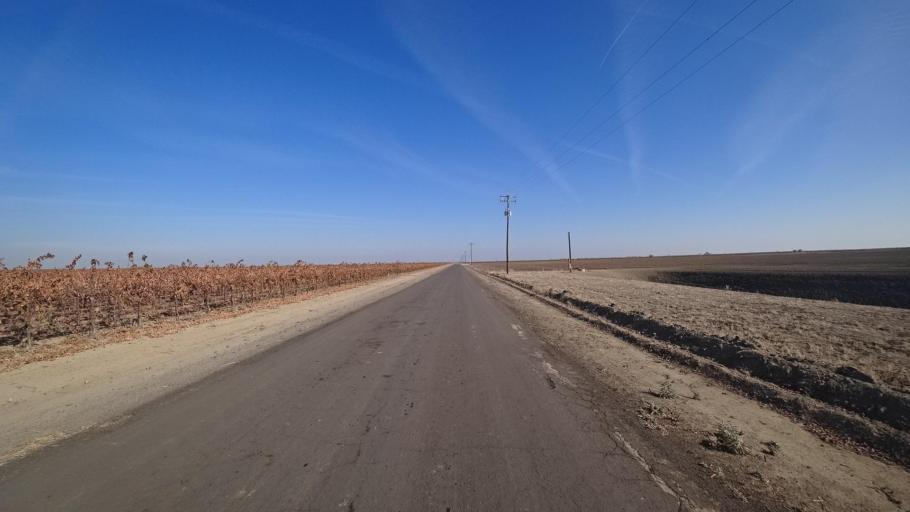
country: US
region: California
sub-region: Kern County
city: Wasco
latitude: 35.6887
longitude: -119.3921
